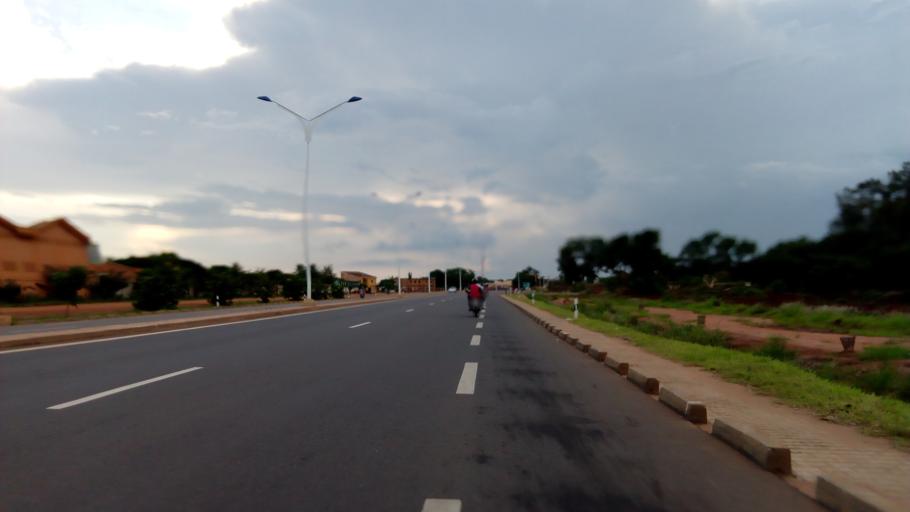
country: TG
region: Maritime
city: Lome
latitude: 6.2447
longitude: 1.1870
